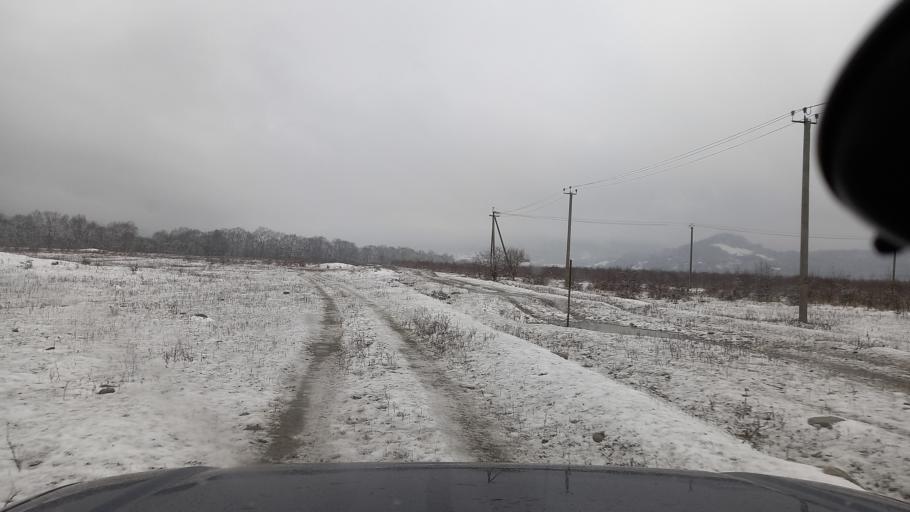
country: RU
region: Adygeya
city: Kamennomostskiy
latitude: 44.2217
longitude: 40.1806
